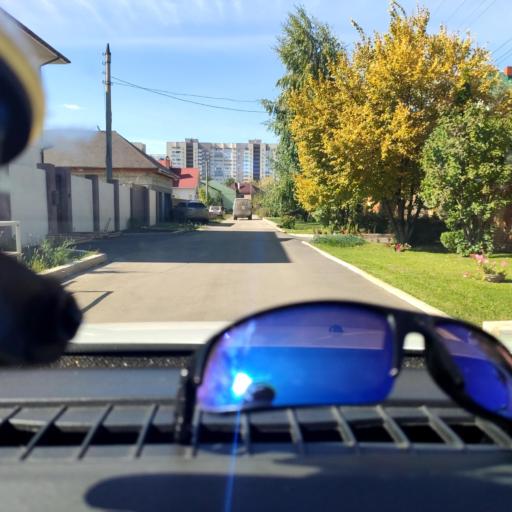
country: RU
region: Samara
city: Samara
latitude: 53.1511
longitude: 50.0820
